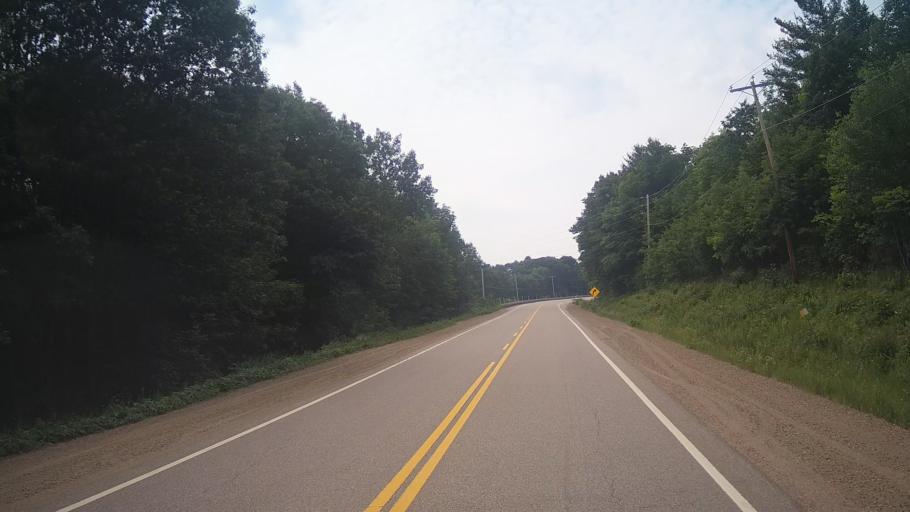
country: CA
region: Ontario
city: Pembroke
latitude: 45.9165
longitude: -76.9435
